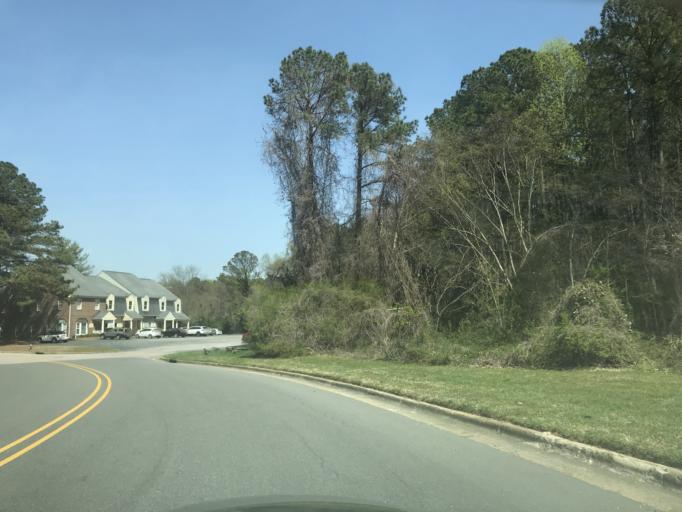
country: US
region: North Carolina
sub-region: Wake County
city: West Raleigh
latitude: 35.8288
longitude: -78.6306
